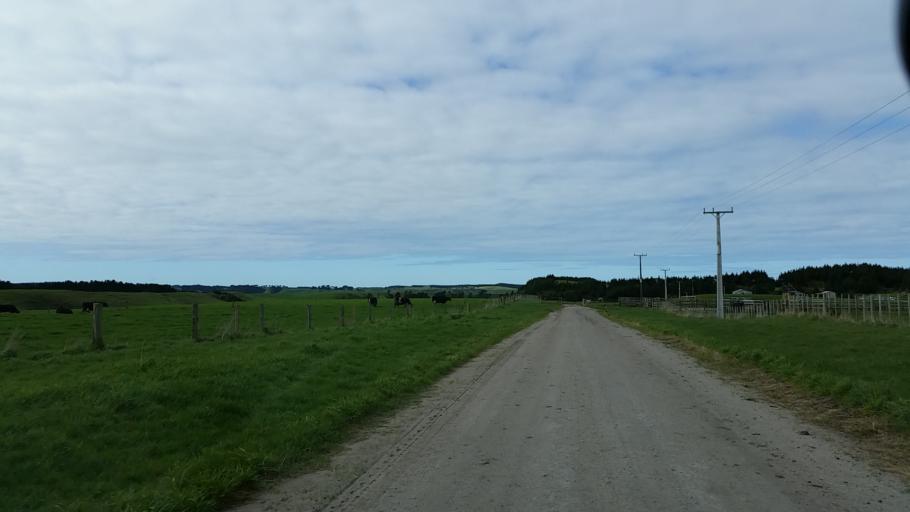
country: NZ
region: Taranaki
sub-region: South Taranaki District
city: Patea
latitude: -39.8073
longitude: 174.6986
